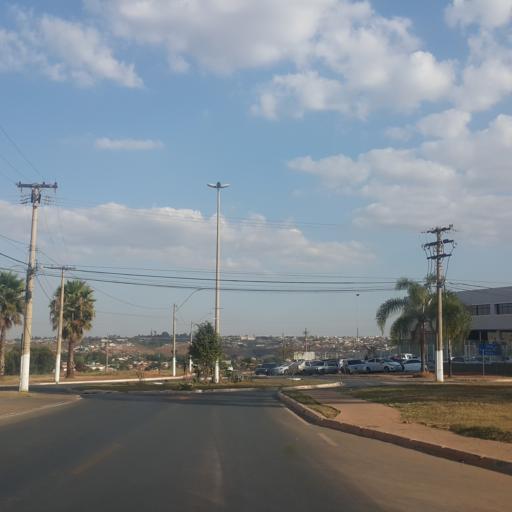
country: BR
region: Federal District
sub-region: Brasilia
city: Brasilia
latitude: -15.8380
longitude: -48.0127
